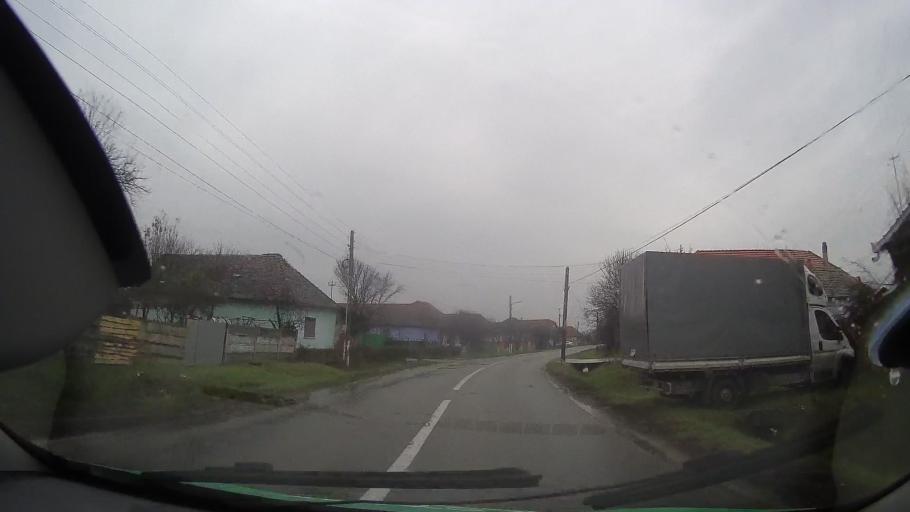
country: RO
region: Bihor
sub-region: Comuna Tulca
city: Tulca
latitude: 46.7880
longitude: 21.8143
